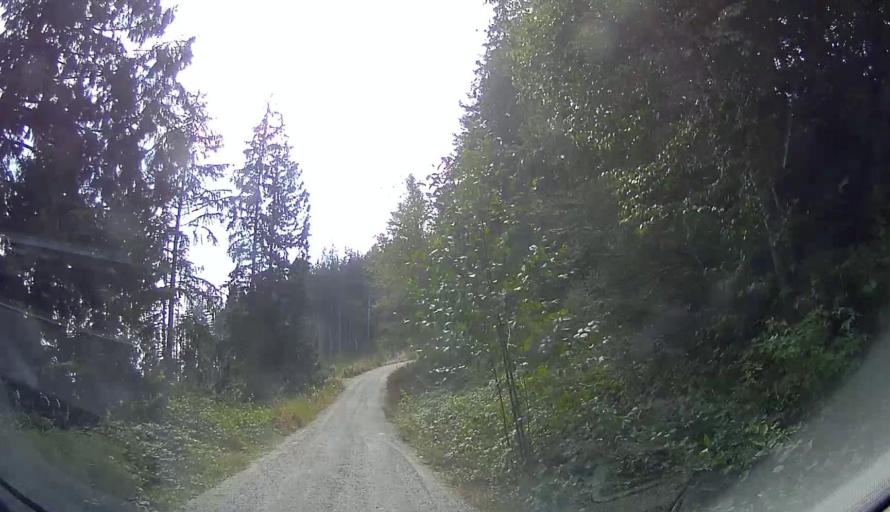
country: US
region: Washington
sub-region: Whatcom County
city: Sudden Valley
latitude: 48.6125
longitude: -122.4213
